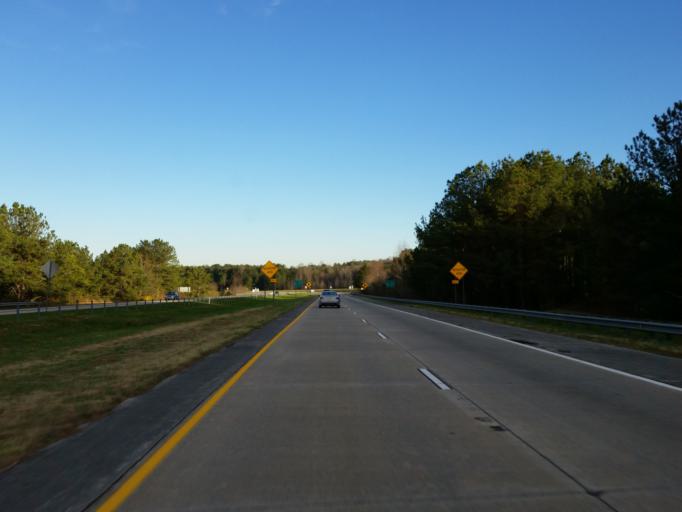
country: US
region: Georgia
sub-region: Pickens County
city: Nelson
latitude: 34.3777
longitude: -84.3929
